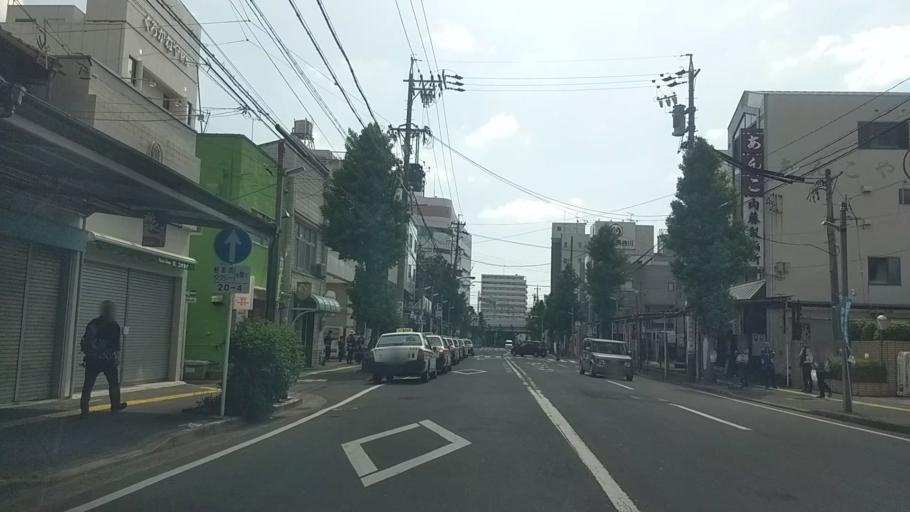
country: JP
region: Shizuoka
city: Hamamatsu
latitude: 34.7030
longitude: 137.7294
